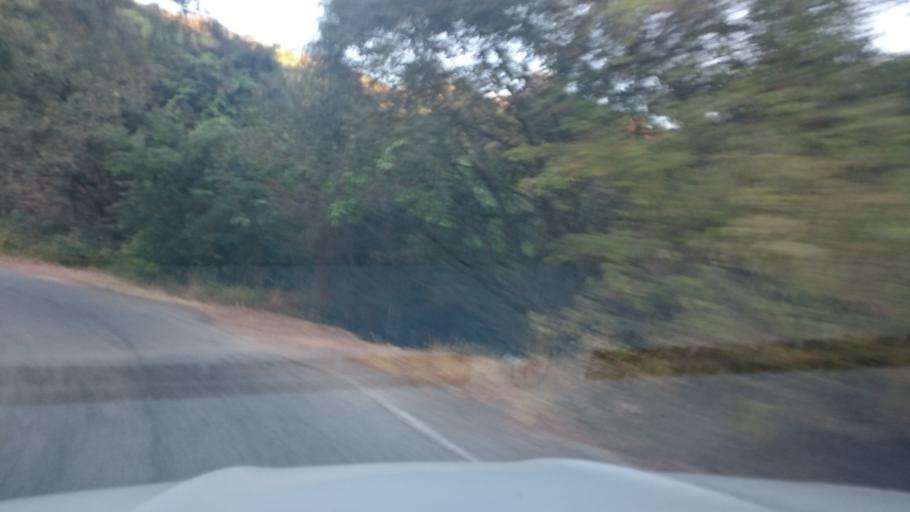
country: BR
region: Rio Grande do Norte
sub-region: Umarizal
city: Umarizal
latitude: -6.0199
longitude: -37.9920
